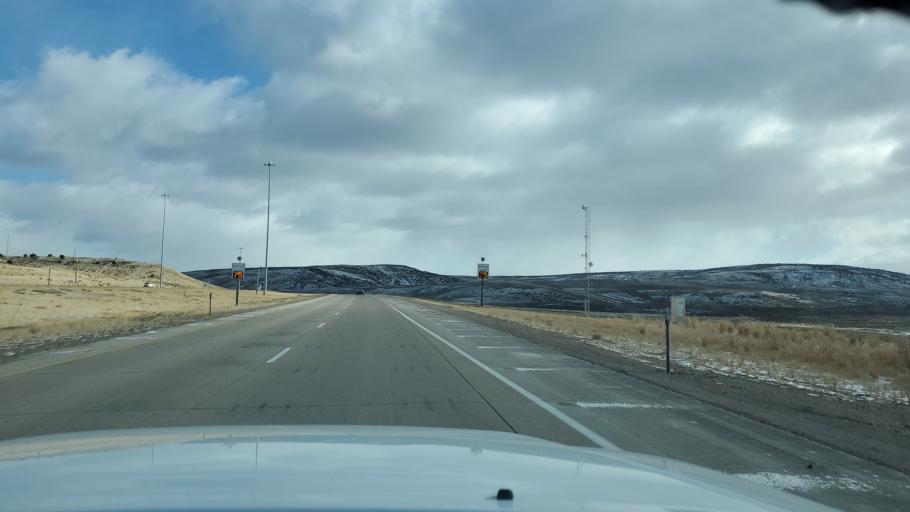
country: US
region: Wyoming
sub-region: Uinta County
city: Evanston
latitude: 41.2623
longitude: -110.8989
